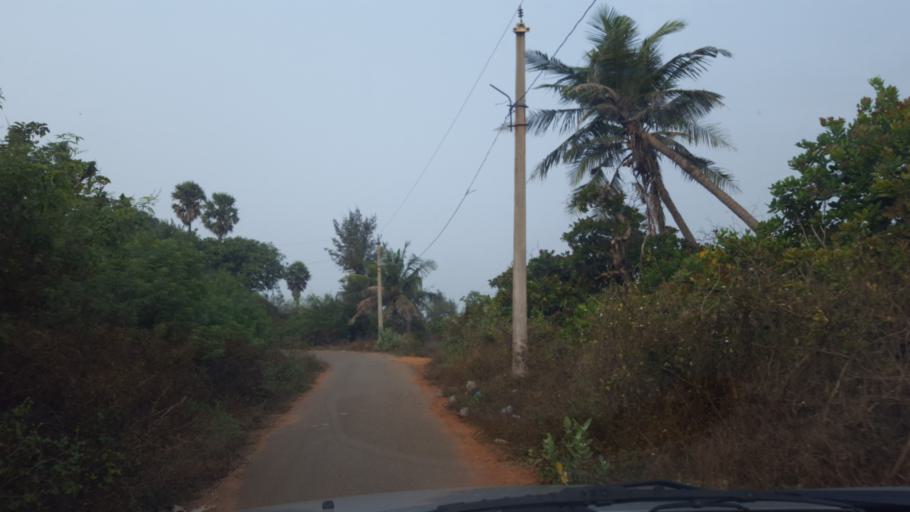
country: IN
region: Andhra Pradesh
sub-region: Srikakulam
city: Palasa
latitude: 18.7594
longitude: 84.5123
